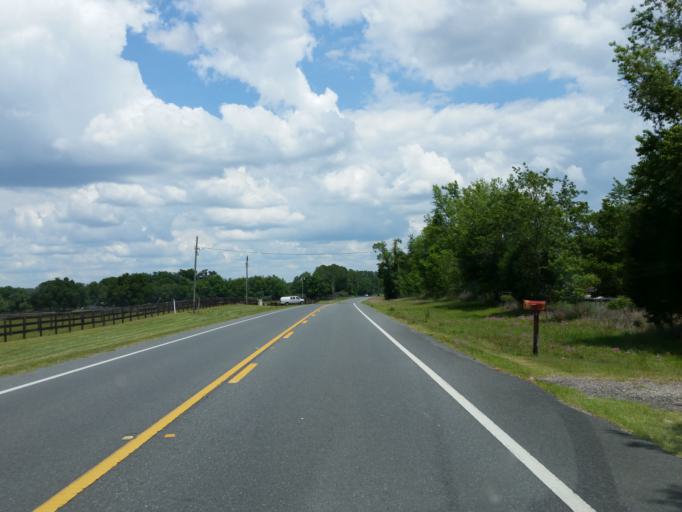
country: US
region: Florida
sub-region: Levy County
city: Williston
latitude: 29.3338
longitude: -82.4554
